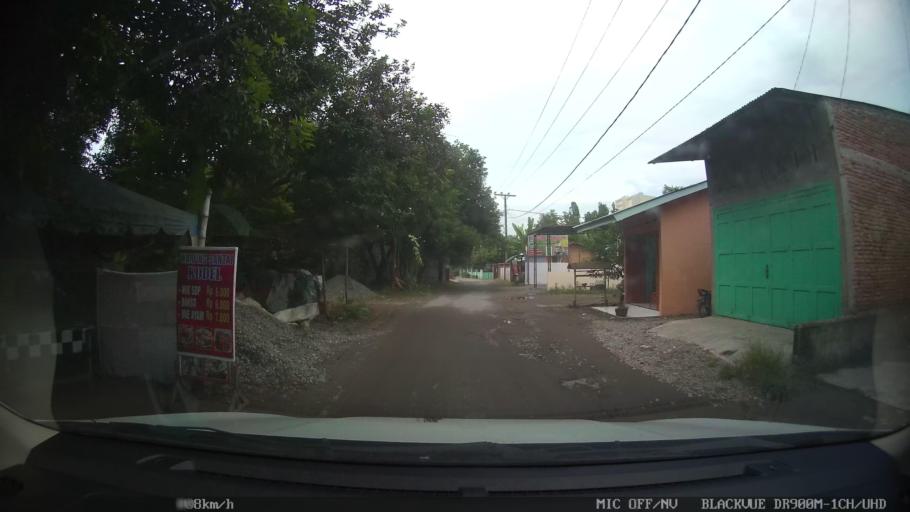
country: ID
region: North Sumatra
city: Sunggal
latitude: 3.6424
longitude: 98.5921
